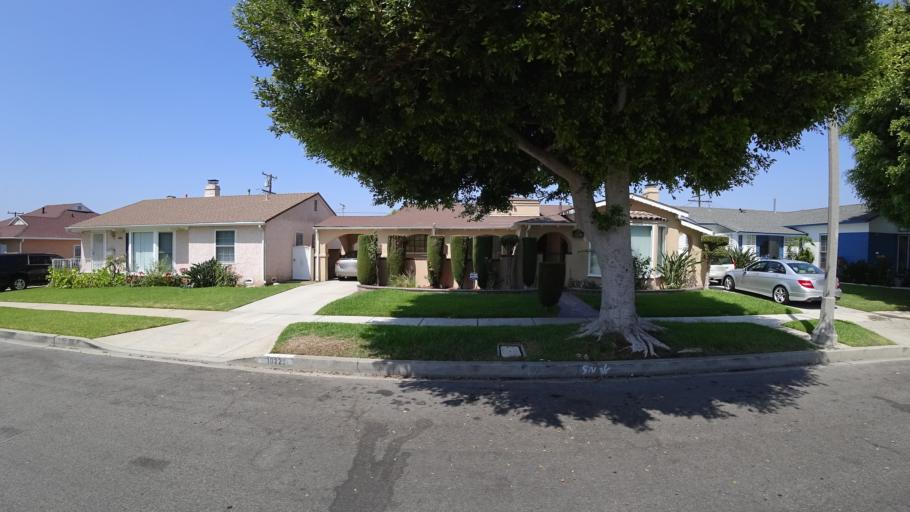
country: US
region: California
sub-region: Los Angeles County
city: Westmont
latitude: 33.9431
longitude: -118.3187
